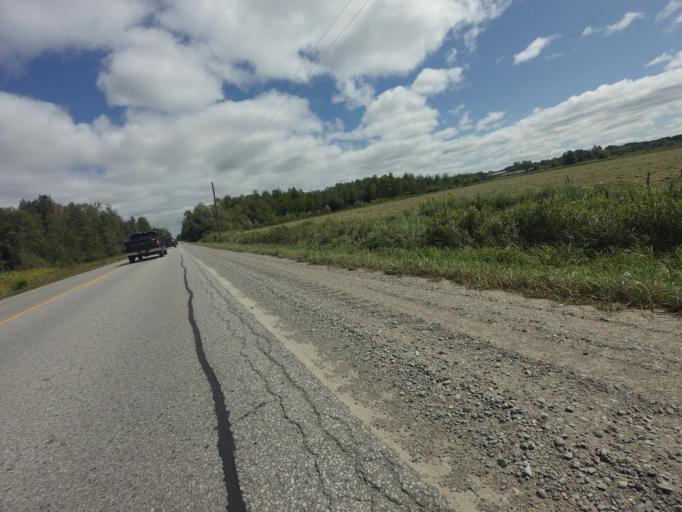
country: CA
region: Ontario
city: Uxbridge
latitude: 44.1179
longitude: -79.2007
